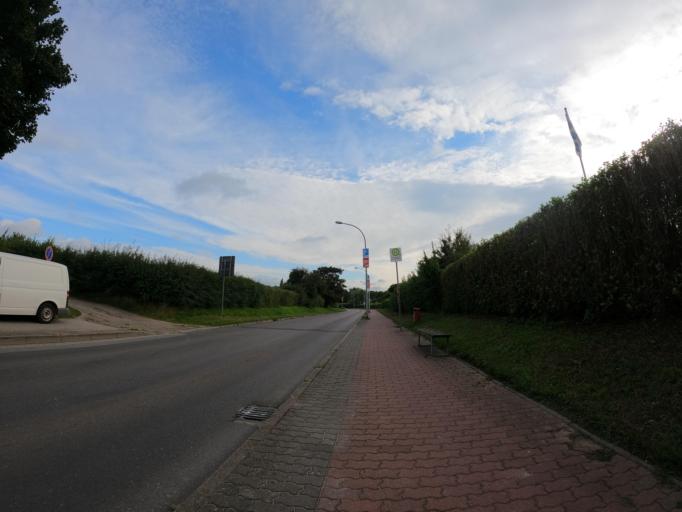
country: DE
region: Mecklenburg-Vorpommern
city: Kramerhof
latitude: 54.3366
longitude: 13.0651
